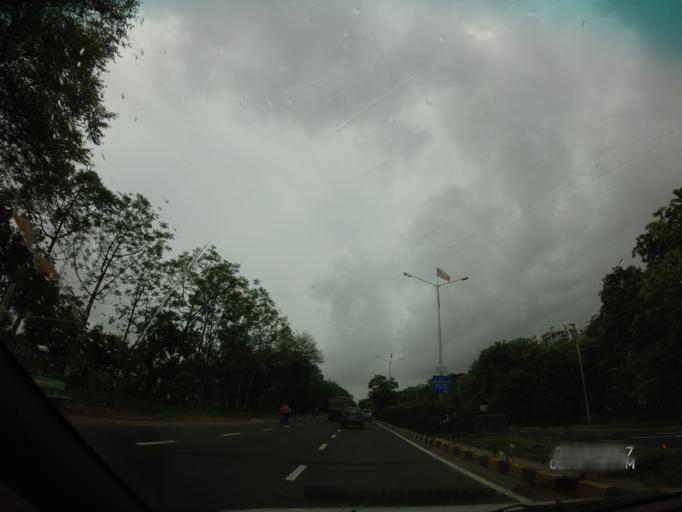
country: IN
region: Gujarat
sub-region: Gandhinagar
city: Adalaj
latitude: 23.1608
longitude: 72.6357
